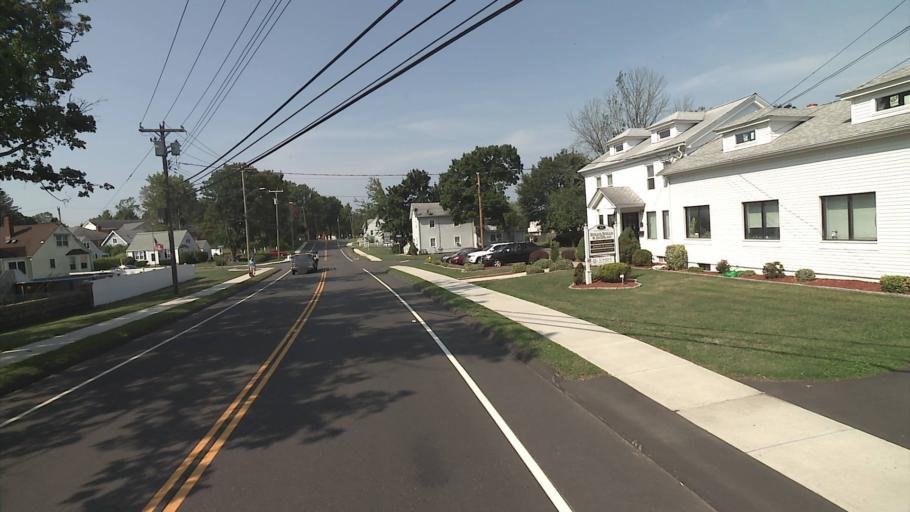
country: US
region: Connecticut
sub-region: New Haven County
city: East Haven
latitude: 41.2769
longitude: -72.8644
